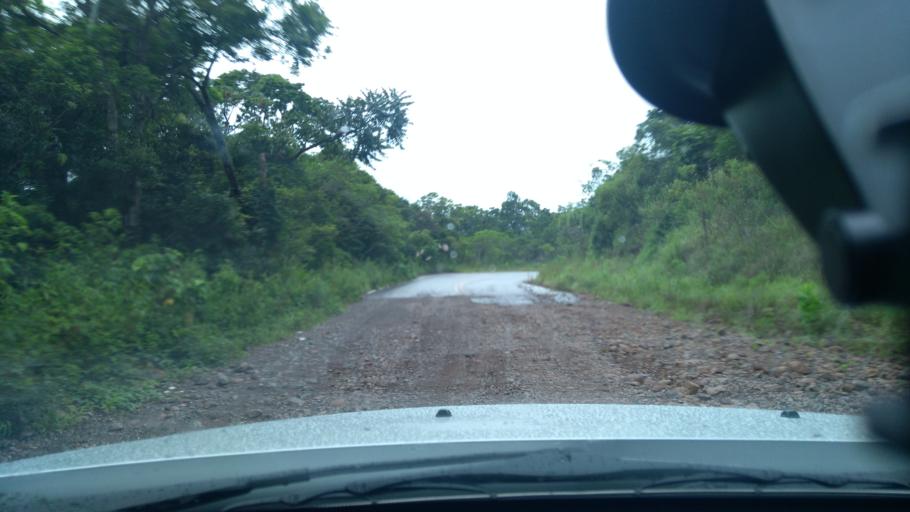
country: BR
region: Rio Grande do Sul
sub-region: Torres
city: Torres
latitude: -29.1905
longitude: -49.9825
